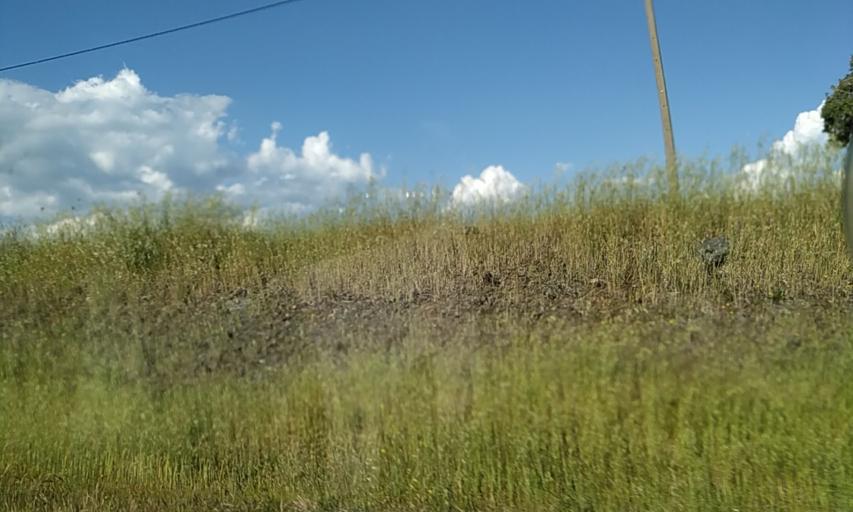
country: PT
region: Portalegre
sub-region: Portalegre
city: Urra
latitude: 39.1298
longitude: -7.4477
